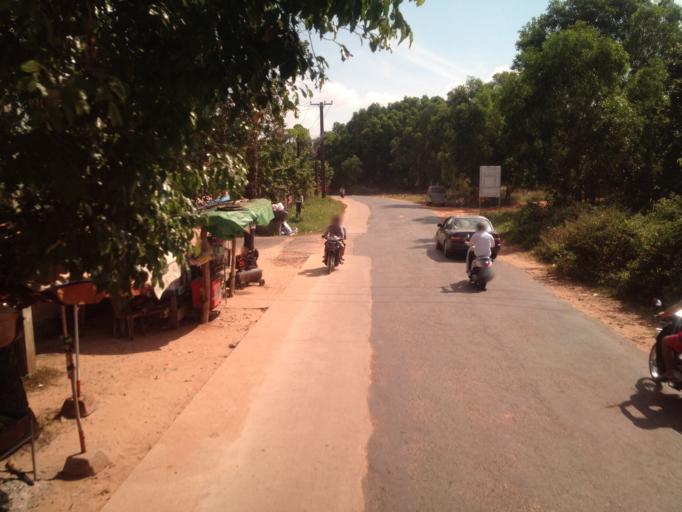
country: KH
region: Preah Sihanouk
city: Sihanoukville
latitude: 10.6338
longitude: 103.5280
